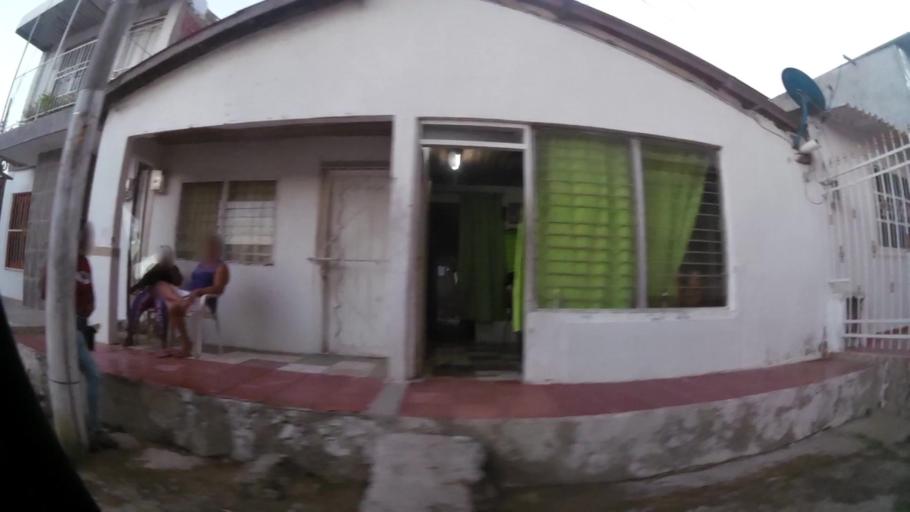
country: CO
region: Bolivar
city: Cartagena
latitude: 10.4103
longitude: -75.5154
